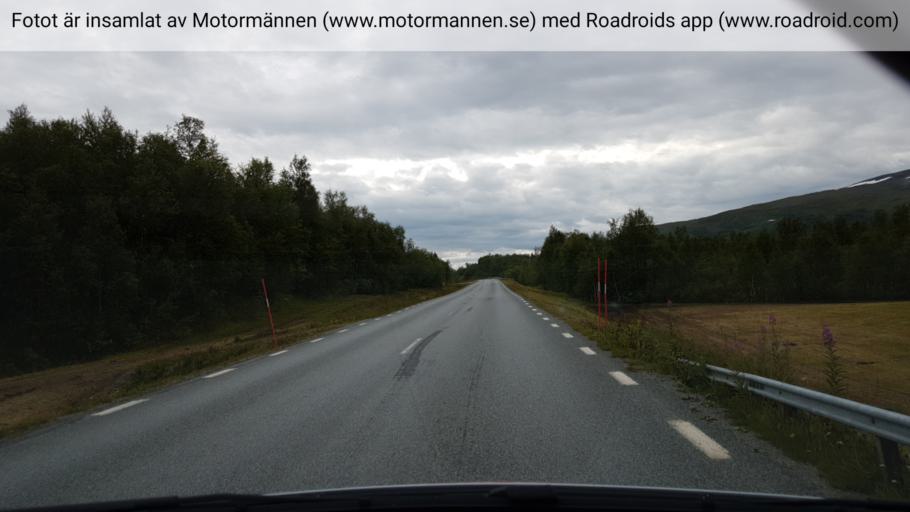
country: NO
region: Nordland
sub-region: Rana
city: Mo i Rana
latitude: 65.8992
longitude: 14.9857
